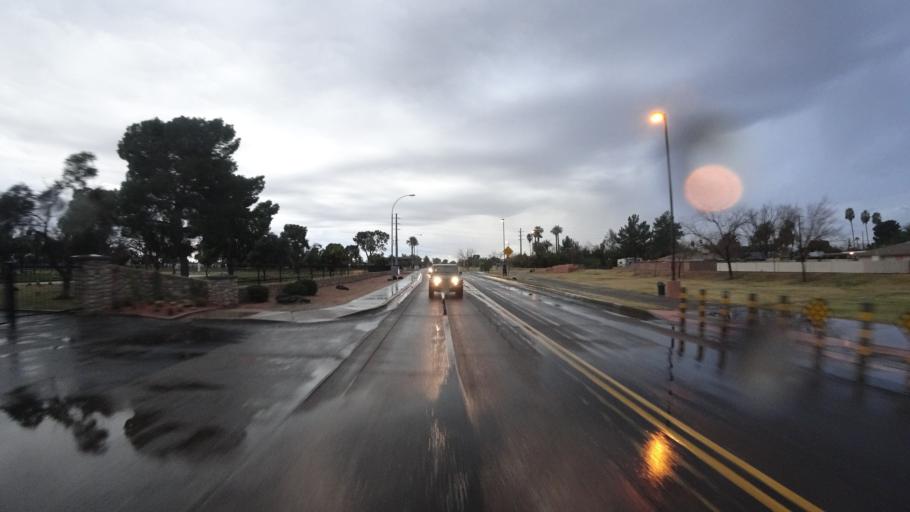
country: US
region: Arizona
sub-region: Maricopa County
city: Paradise Valley
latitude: 33.4738
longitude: -111.9781
